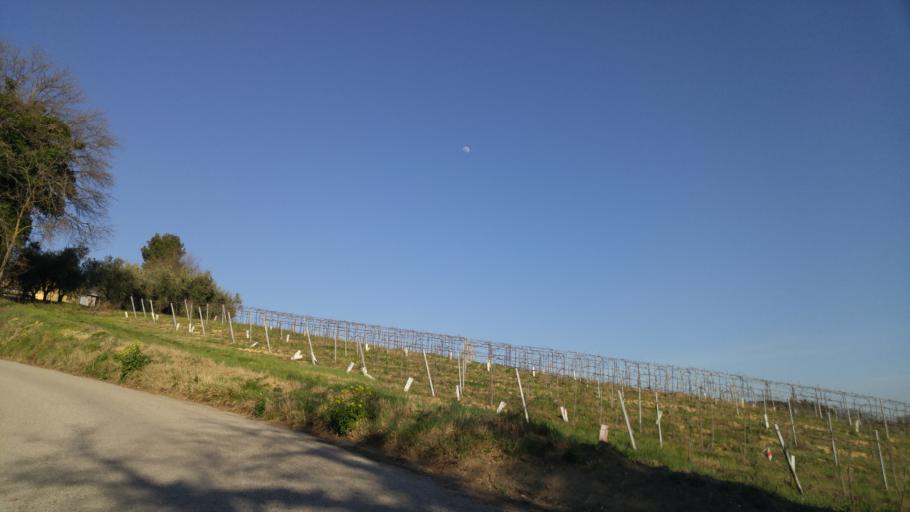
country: IT
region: The Marches
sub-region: Provincia di Pesaro e Urbino
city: Fenile
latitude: 43.8484
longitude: 12.9193
